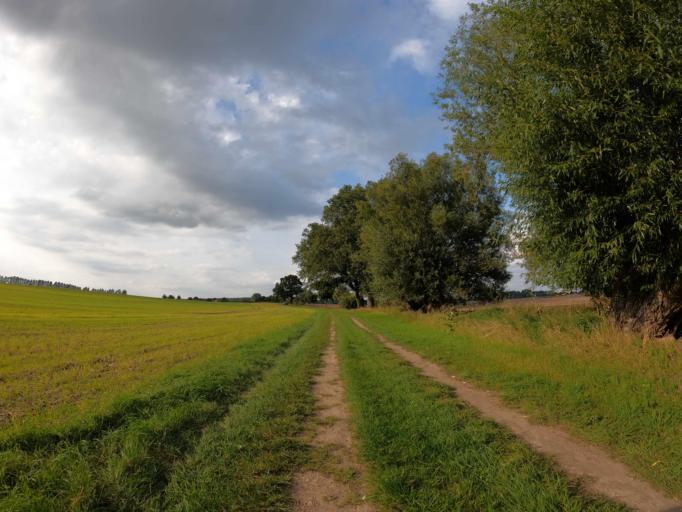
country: DE
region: Mecklenburg-Vorpommern
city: Klink
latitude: 53.4485
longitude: 12.5238
